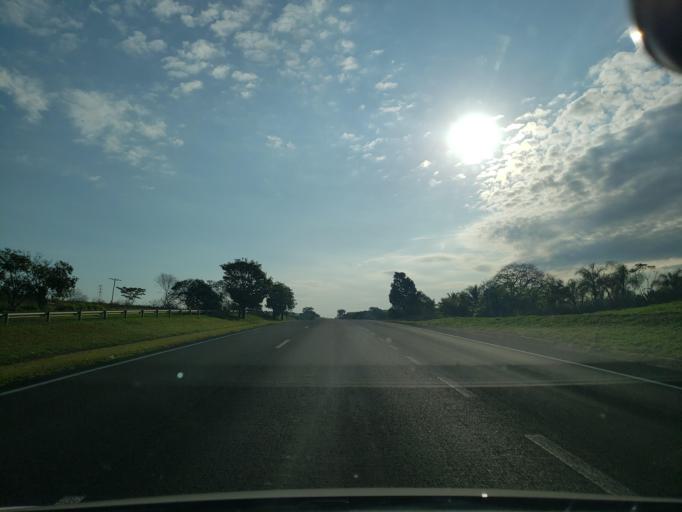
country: BR
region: Sao Paulo
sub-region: Valparaiso
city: Valparaiso
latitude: -21.2081
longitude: -50.8783
